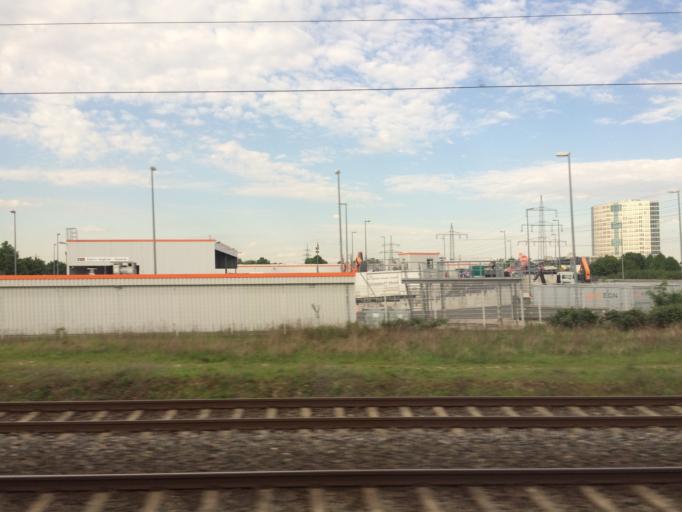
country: DE
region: North Rhine-Westphalia
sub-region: Regierungsbezirk Koln
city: Gremberghoven
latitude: 50.9080
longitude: 7.0476
